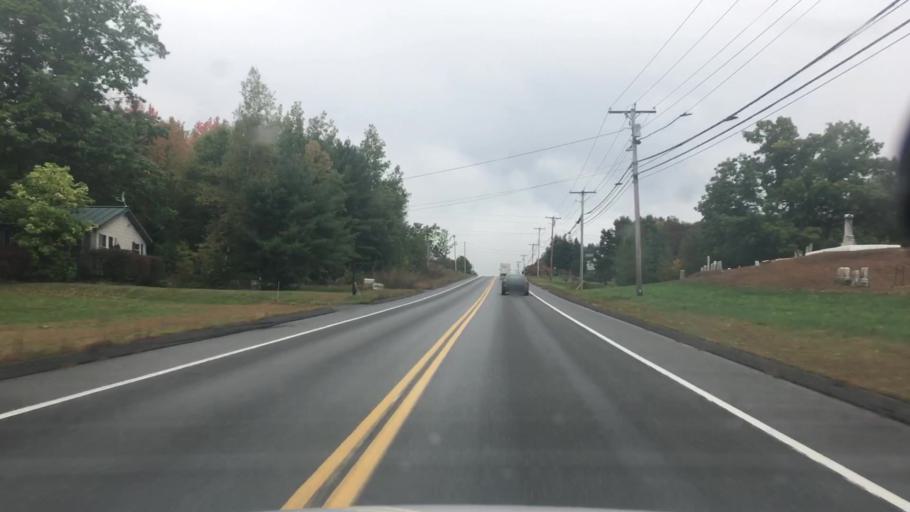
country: US
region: Maine
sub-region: Kennebec County
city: Augusta
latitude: 44.3632
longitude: -69.7873
